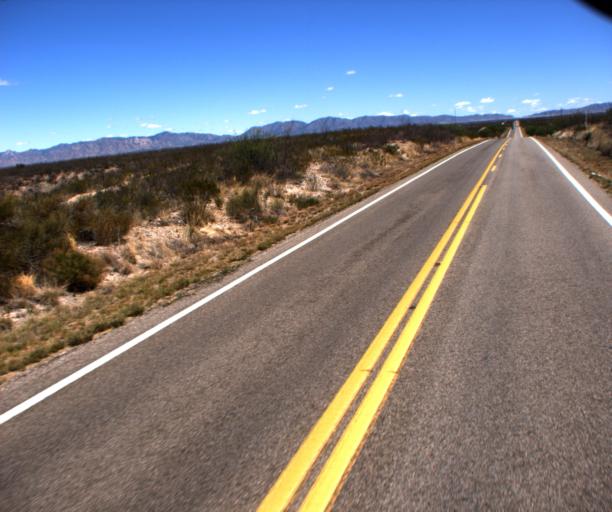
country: US
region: Arizona
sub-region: Cochise County
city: Tombstone
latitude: 31.7436
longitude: -110.1385
